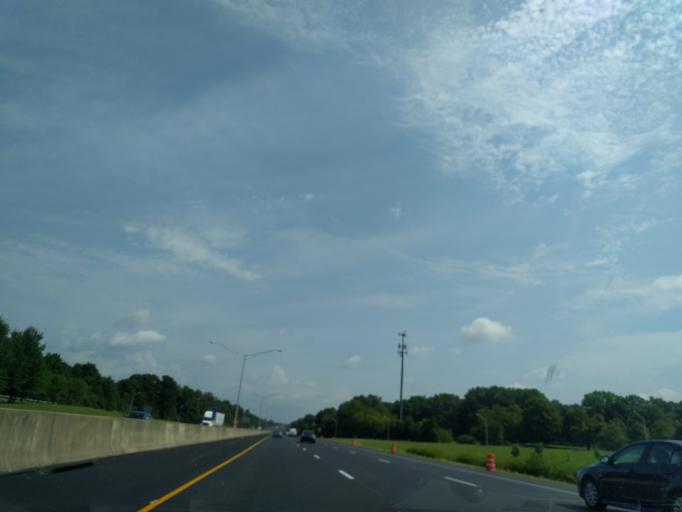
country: US
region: Kentucky
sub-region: Warren County
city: Bowling Green
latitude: 36.9781
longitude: -86.3907
